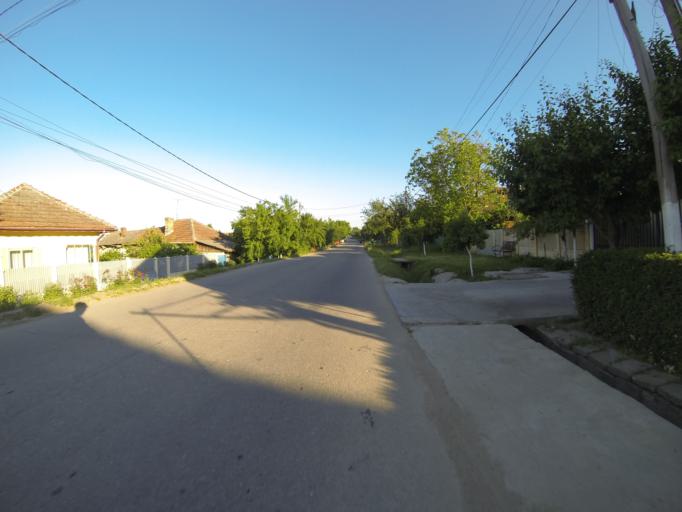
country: RO
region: Dolj
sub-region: Comuna Tuglui
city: Tuglui
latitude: 44.2099
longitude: 23.7942
